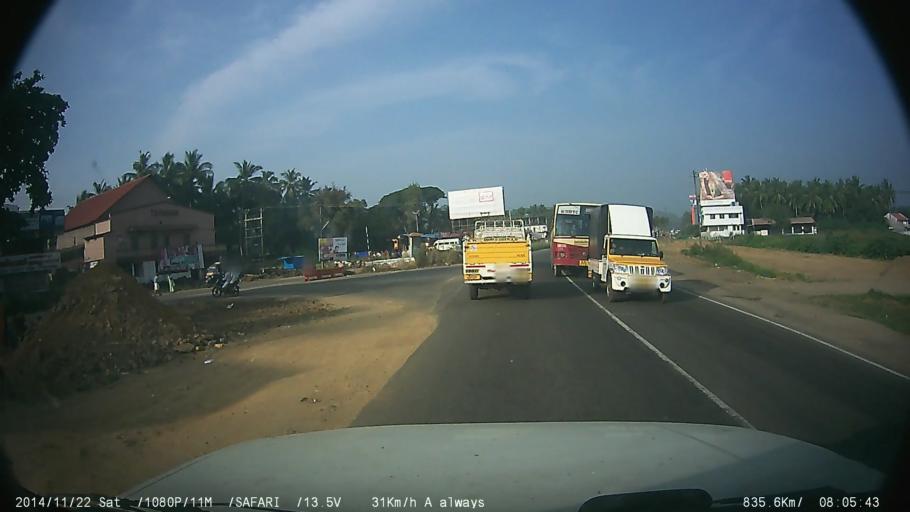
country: IN
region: Kerala
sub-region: Thrissur District
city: Chelakara
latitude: 10.5908
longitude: 76.4769
